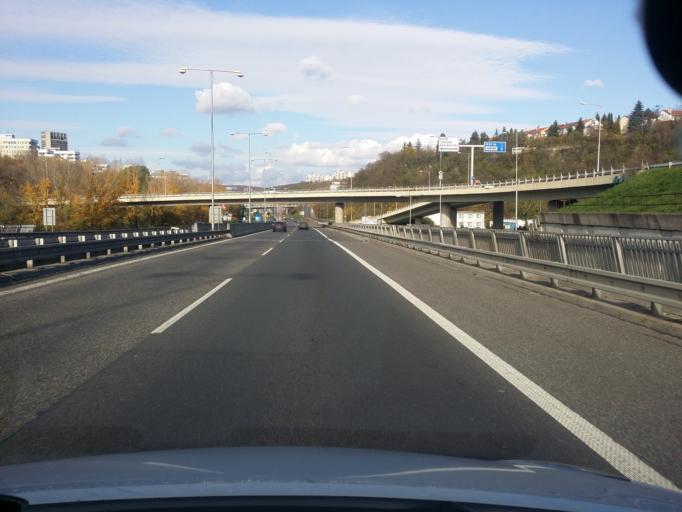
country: SK
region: Bratislavsky
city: Bratislava
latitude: 48.1473
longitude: 17.0762
